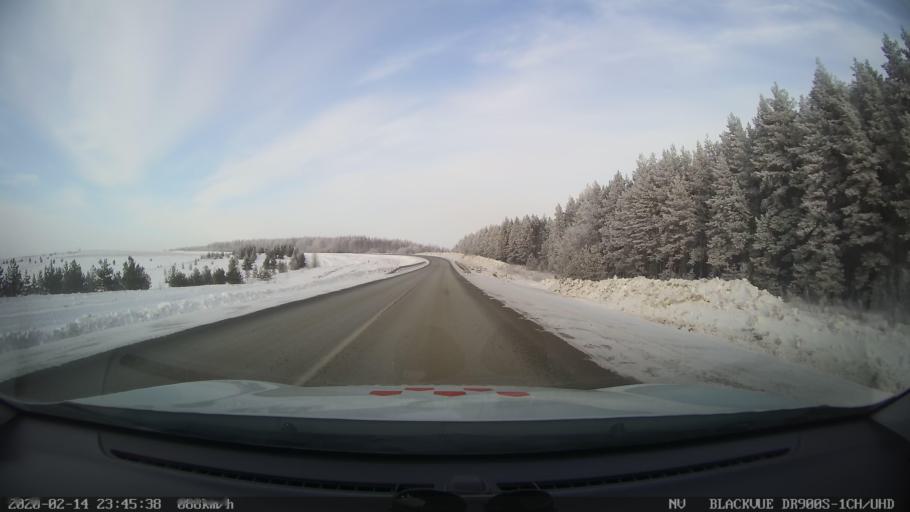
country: RU
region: Tatarstan
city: Kuybyshevskiy Zaton
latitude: 55.2233
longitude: 49.2330
